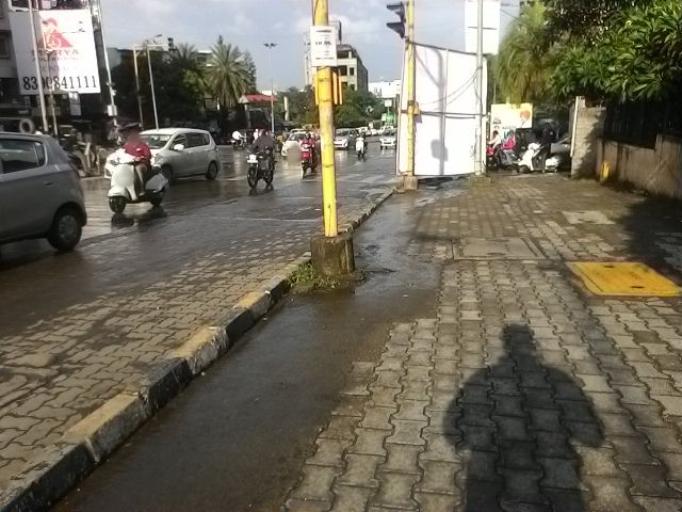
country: IN
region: Maharashtra
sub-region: Pune Division
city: Khadki
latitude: 18.5548
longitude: 73.7973
